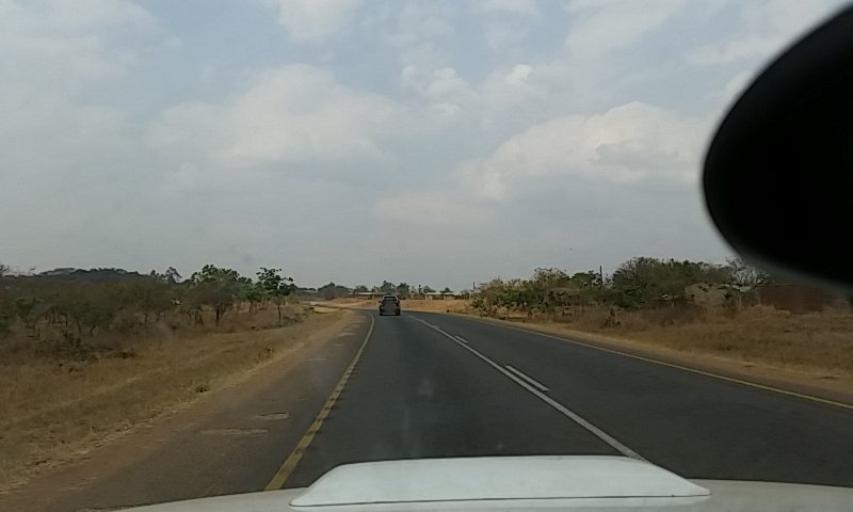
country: MW
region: Central Region
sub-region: Lilongwe District
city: Lilongwe
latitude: -13.8416
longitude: 33.8469
